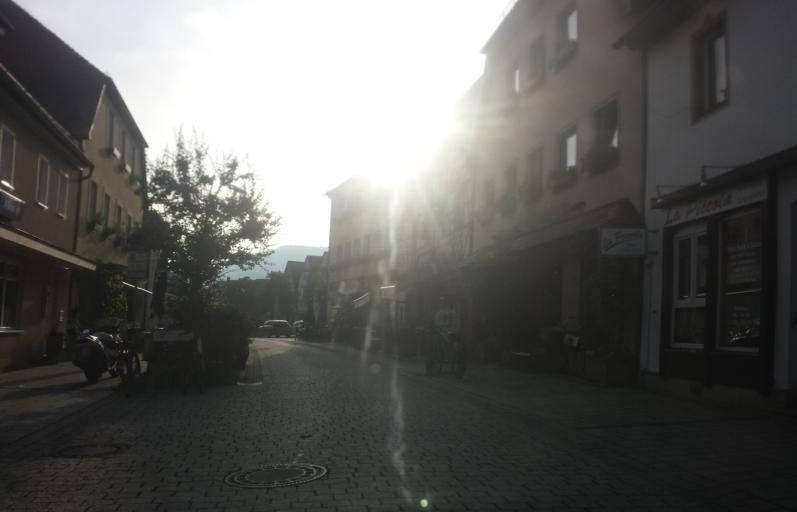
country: DE
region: Bavaria
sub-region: Upper Franconia
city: Ebermannstadt
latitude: 49.7799
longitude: 11.1862
